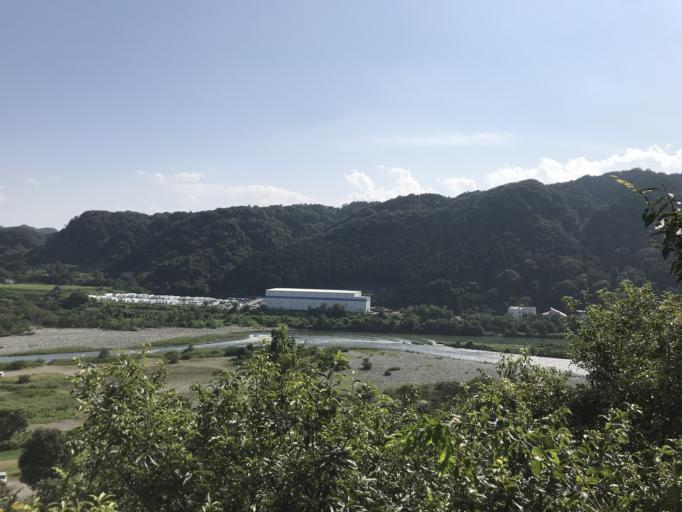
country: JP
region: Tokyo
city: Hachioji
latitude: 35.5754
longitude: 139.3123
